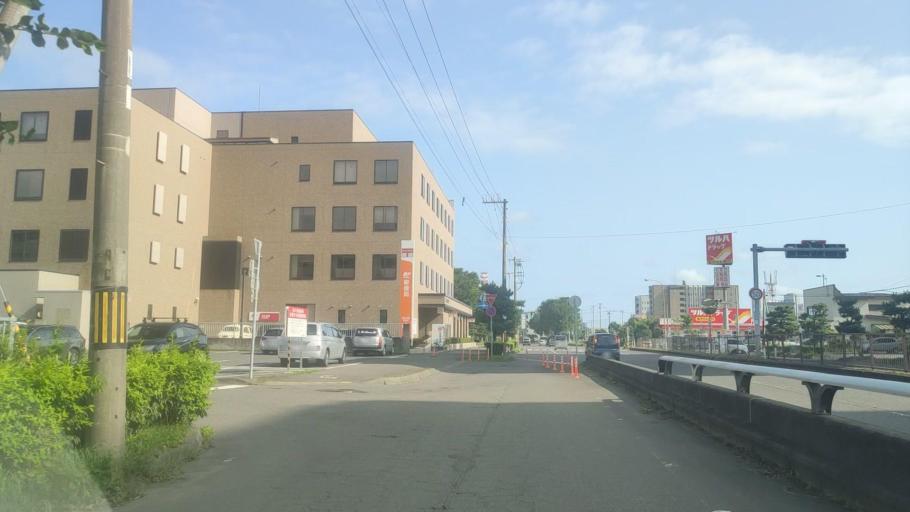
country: JP
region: Hokkaido
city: Tomakomai
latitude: 42.6395
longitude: 141.6016
